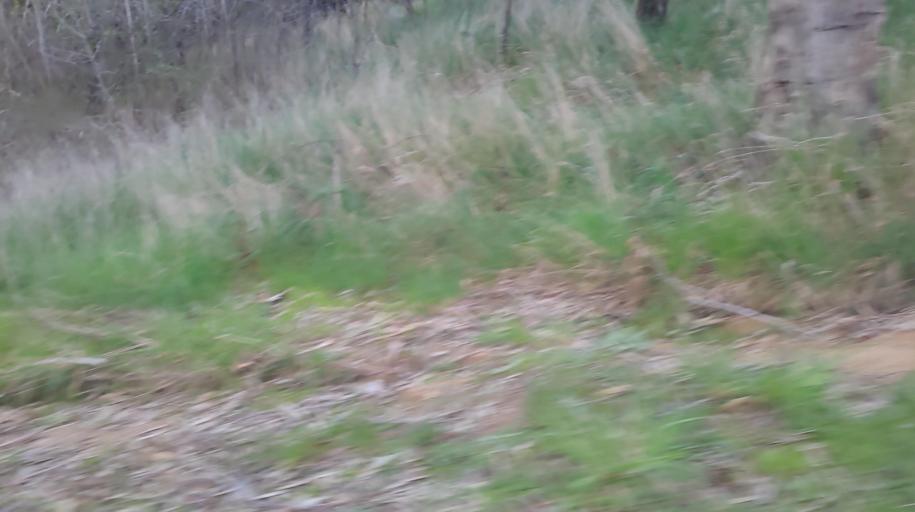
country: AU
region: New South Wales
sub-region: Blayney
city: Millthorpe
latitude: -33.4045
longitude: 149.3126
